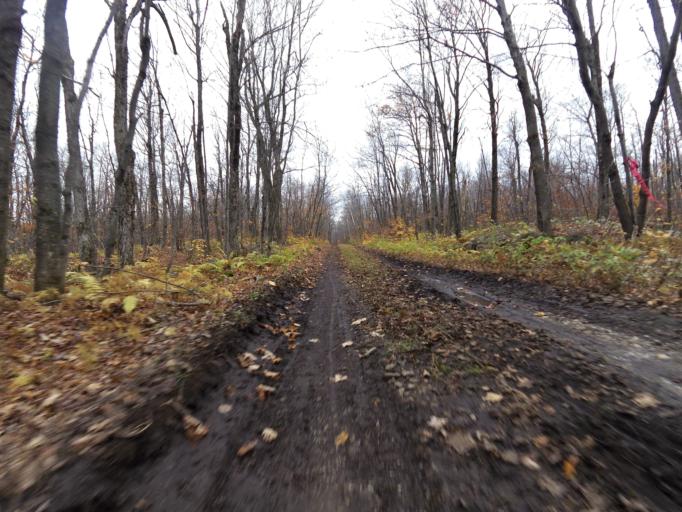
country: CA
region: Quebec
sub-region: Outaouais
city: Wakefield
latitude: 45.5541
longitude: -75.9748
